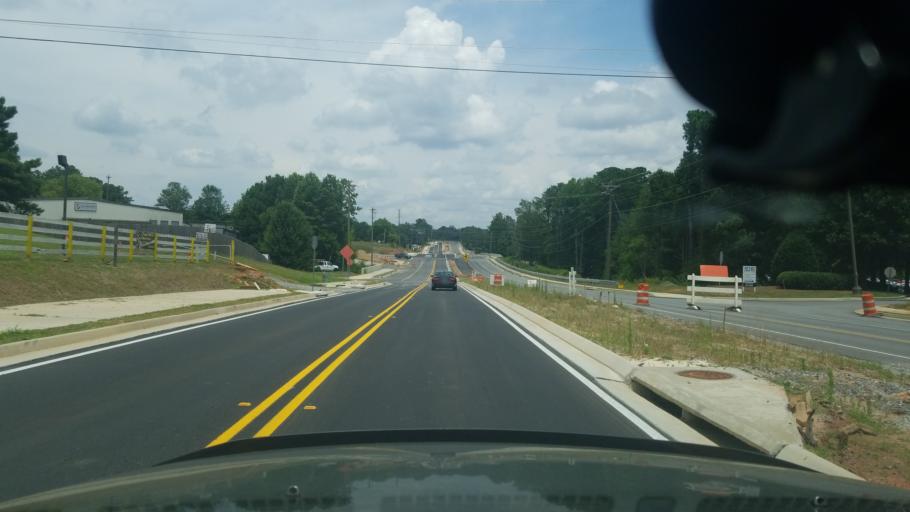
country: US
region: Georgia
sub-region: Fulton County
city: Alpharetta
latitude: 34.1106
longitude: -84.2369
